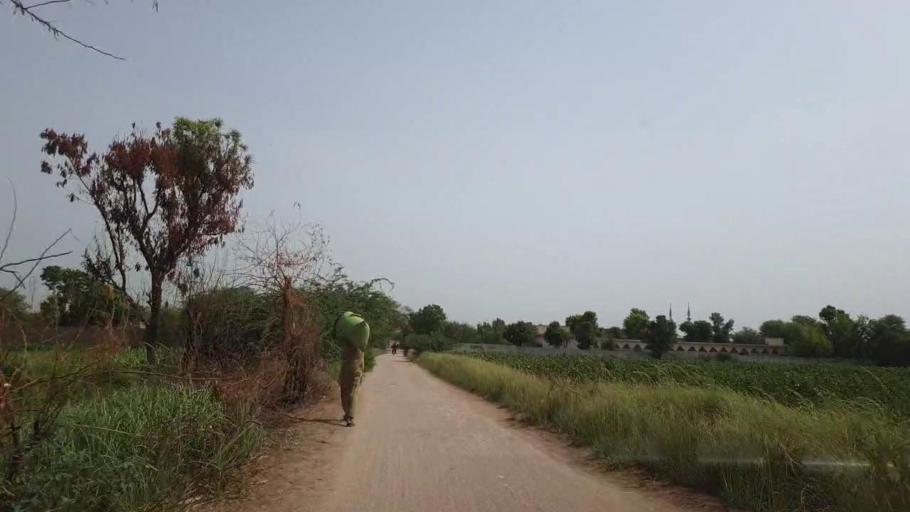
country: PK
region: Sindh
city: Sakrand
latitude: 26.1143
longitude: 68.3975
